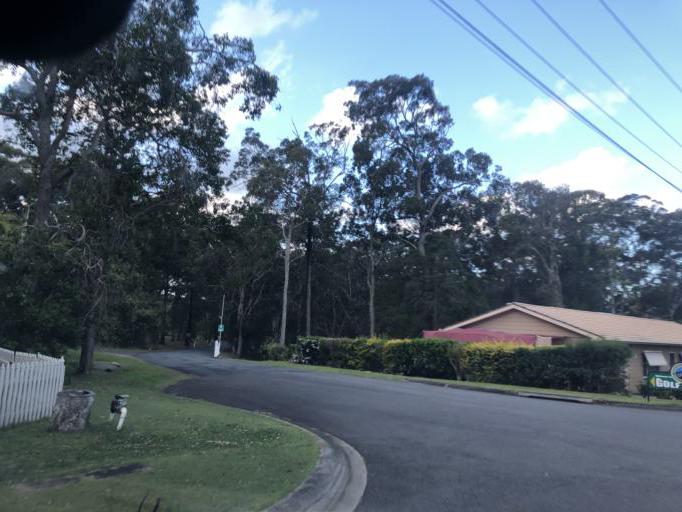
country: AU
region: New South Wales
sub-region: Coffs Harbour
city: Woolgoolga
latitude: -30.0962
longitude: 153.1942
